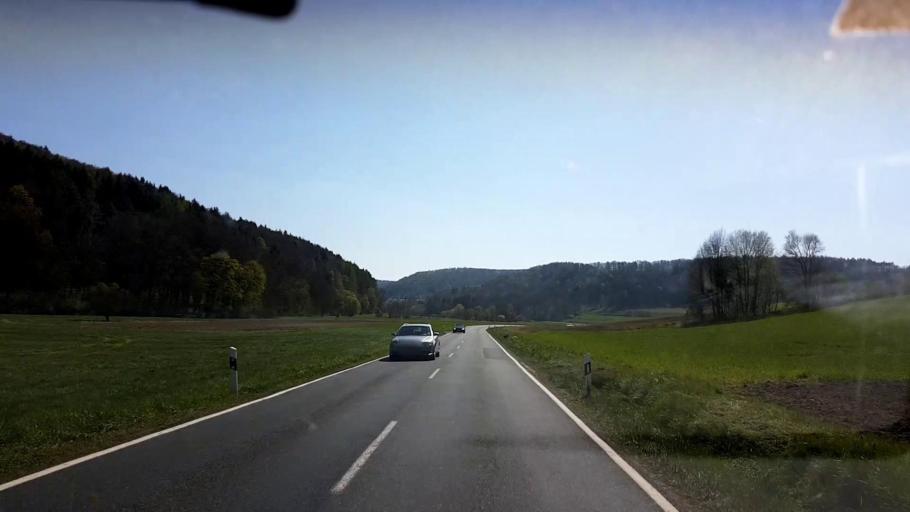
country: DE
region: Bavaria
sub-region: Upper Franconia
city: Unterleinleiter
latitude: 49.8373
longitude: 11.1924
